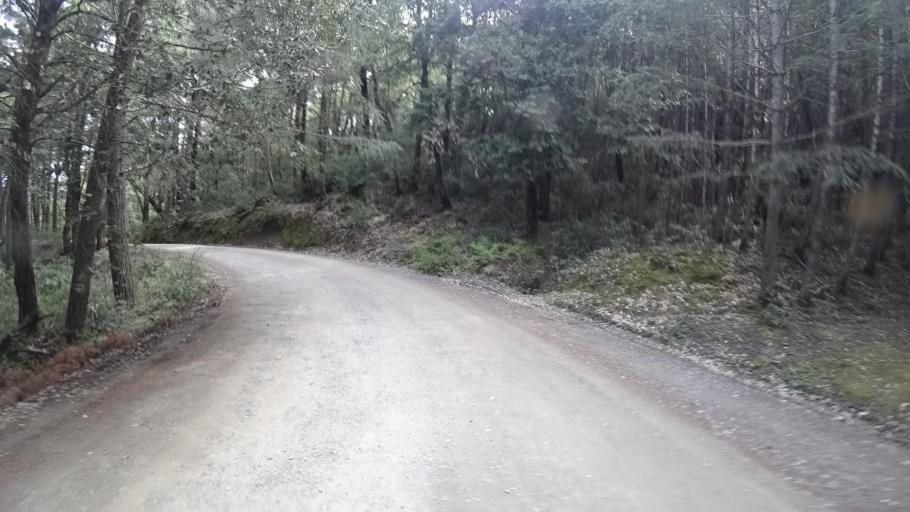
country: US
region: California
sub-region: Humboldt County
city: Redway
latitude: 40.0431
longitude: -123.8427
